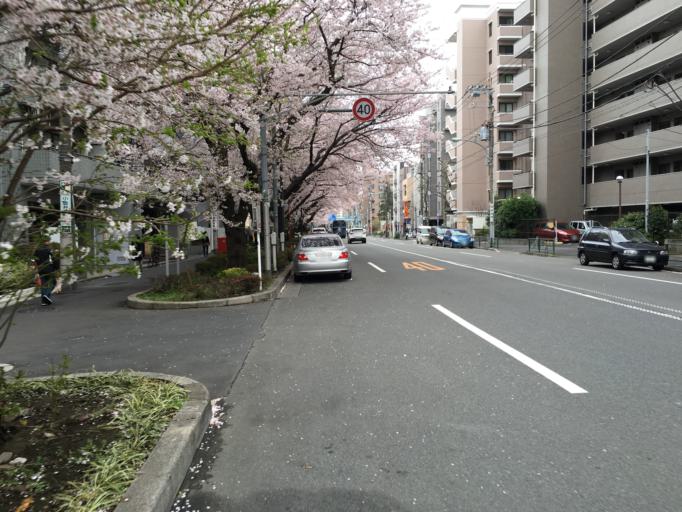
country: JP
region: Saitama
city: Wako
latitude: 35.7355
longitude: 139.6336
